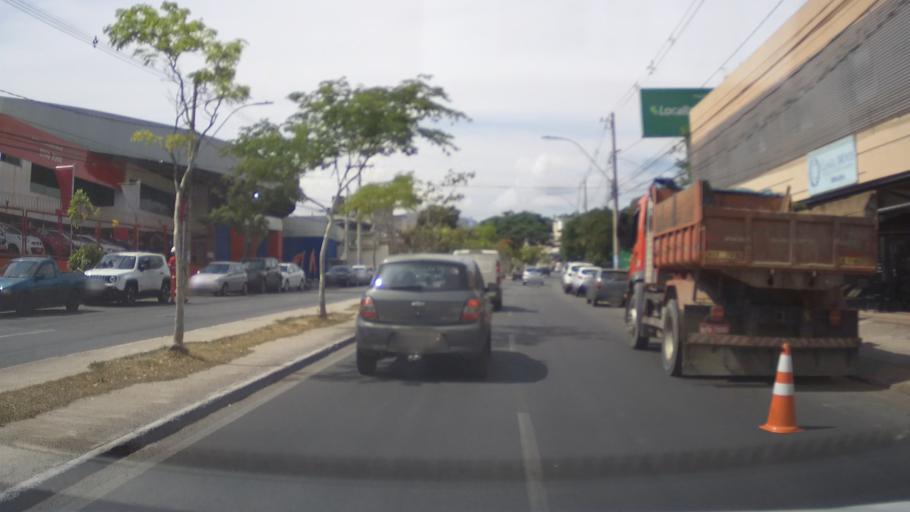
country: BR
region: Minas Gerais
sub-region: Belo Horizonte
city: Belo Horizonte
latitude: -19.9453
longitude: -43.9695
